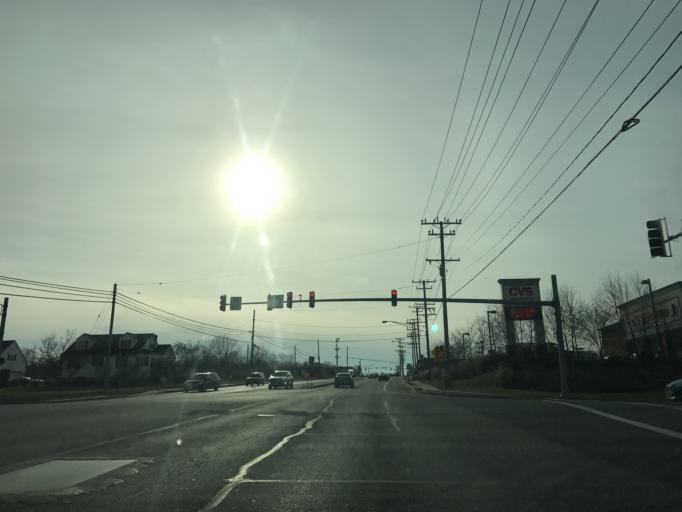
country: US
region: Maryland
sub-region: Baltimore County
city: Perry Hall
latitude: 39.4197
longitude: -76.4556
